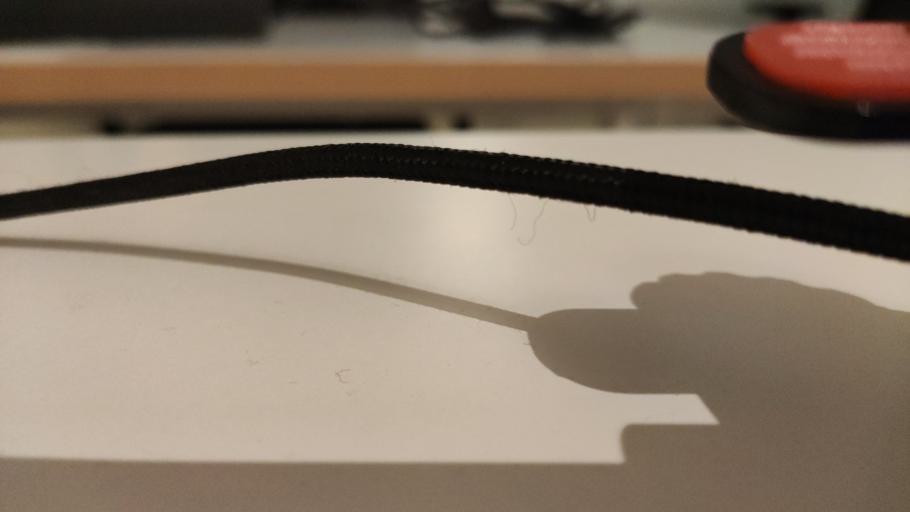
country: RU
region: Moskovskaya
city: Rybnoye
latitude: 56.4183
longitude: 37.7102
